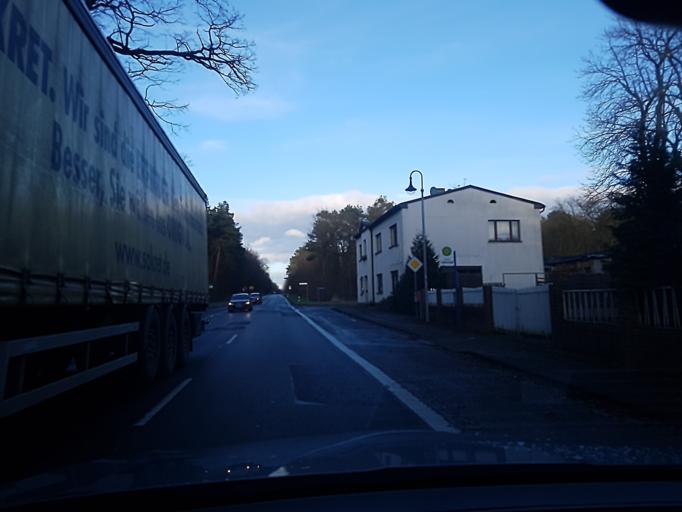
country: DE
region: Brandenburg
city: Trobitz
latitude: 51.5752
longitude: 13.4279
